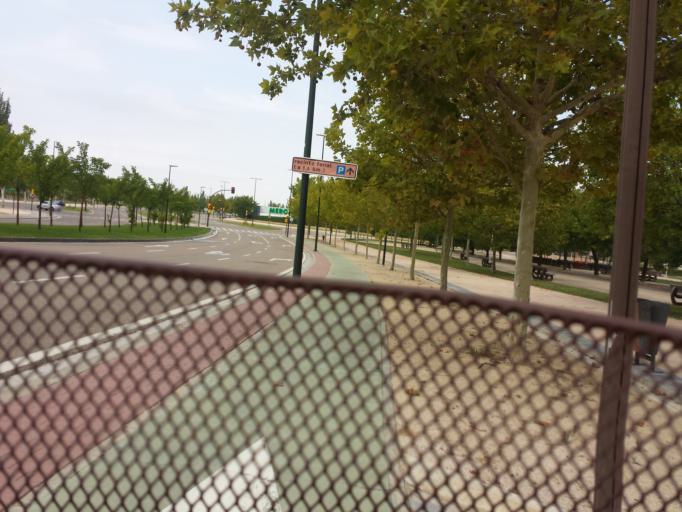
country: ES
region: Aragon
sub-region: Provincia de Zaragoza
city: Montecanal
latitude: 41.6216
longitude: -0.9343
